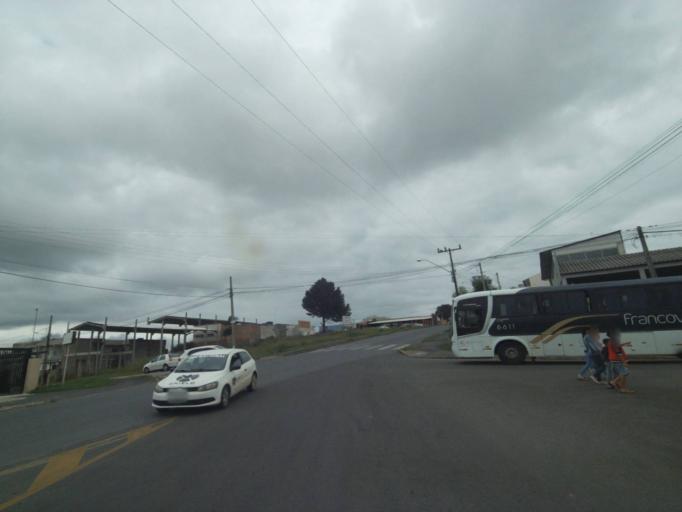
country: BR
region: Parana
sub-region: Quatro Barras
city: Quatro Barras
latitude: -25.3542
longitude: -49.1107
